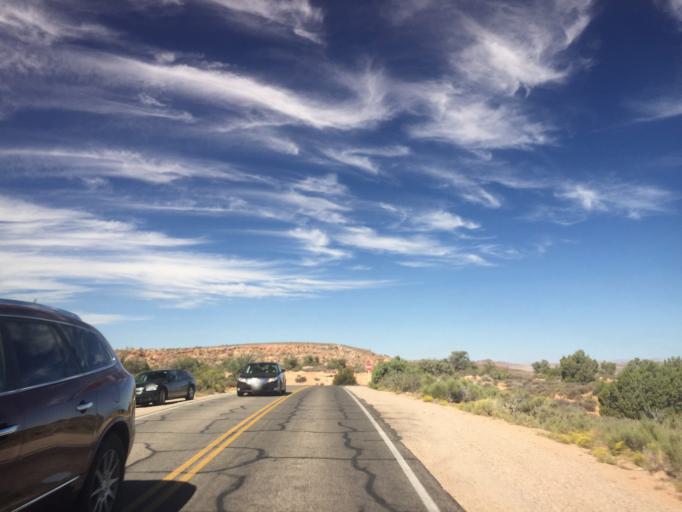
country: US
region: Utah
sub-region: Grand County
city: Moab
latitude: 38.7035
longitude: -109.5624
